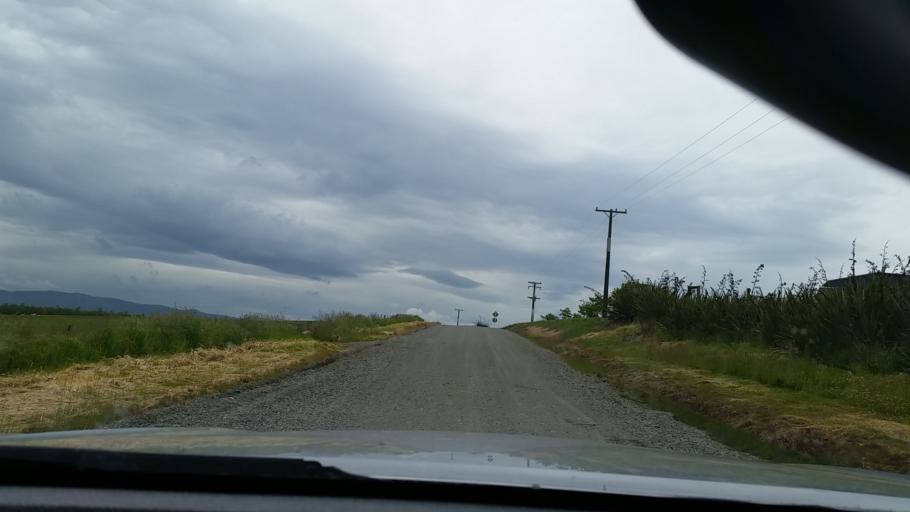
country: NZ
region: Southland
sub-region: Southland District
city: Winton
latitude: -45.9067
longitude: 168.1467
